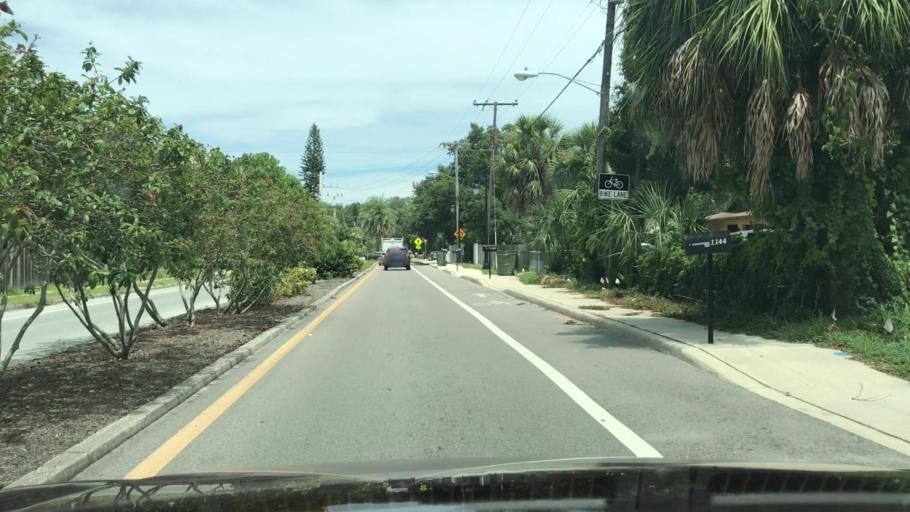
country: US
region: Florida
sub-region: Sarasota County
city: North Sarasota
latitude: 27.3672
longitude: -82.5482
